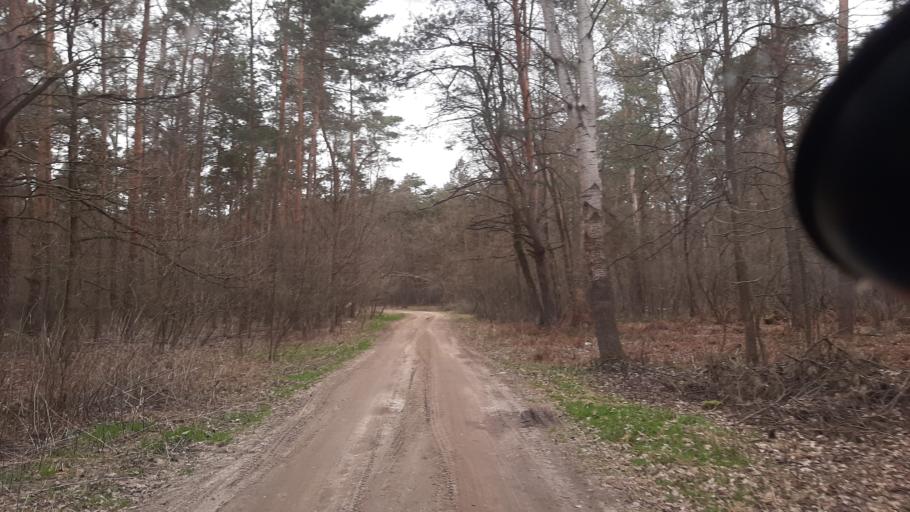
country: PL
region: Lublin Voivodeship
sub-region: Powiat lubartowski
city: Abramow
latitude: 51.4424
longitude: 22.3450
